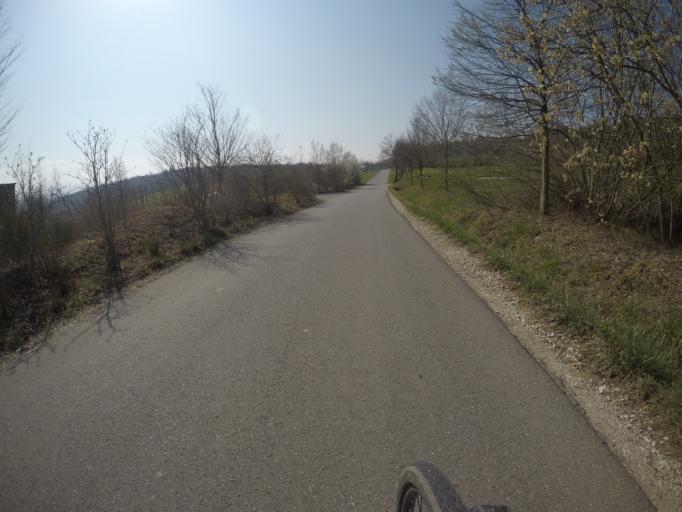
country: DE
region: Baden-Wuerttemberg
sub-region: Regierungsbezirk Stuttgart
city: Altenriet
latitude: 48.5761
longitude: 9.2192
